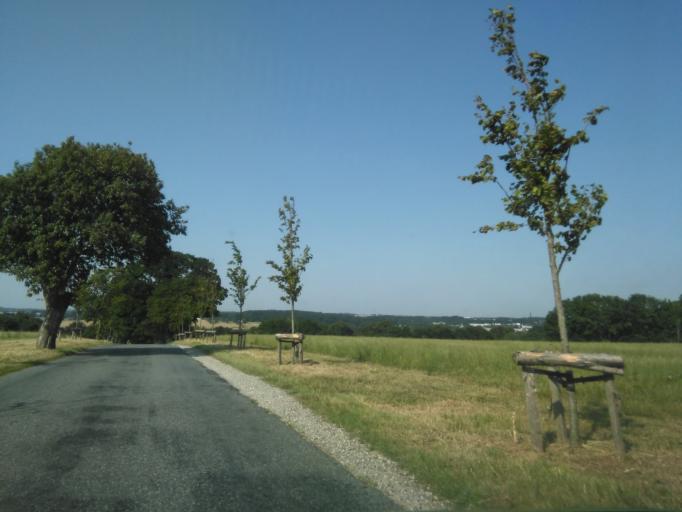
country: DK
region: Central Jutland
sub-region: Arhus Kommune
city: Kolt
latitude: 56.1345
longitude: 10.0781
